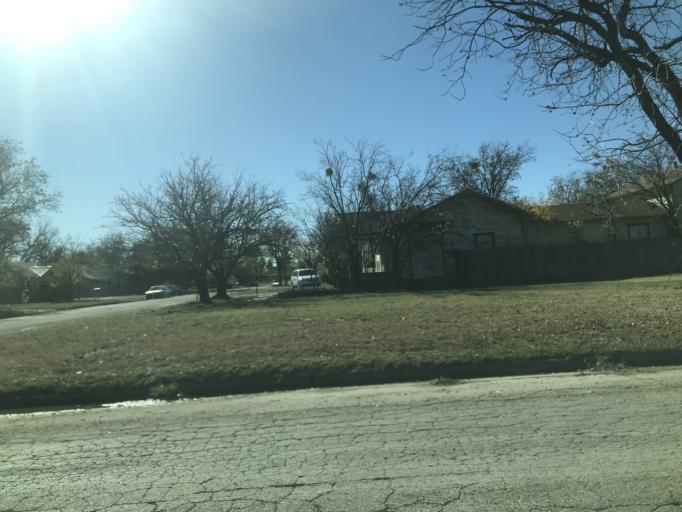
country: US
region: Texas
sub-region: Taylor County
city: Abilene
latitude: 32.4638
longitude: -99.7342
